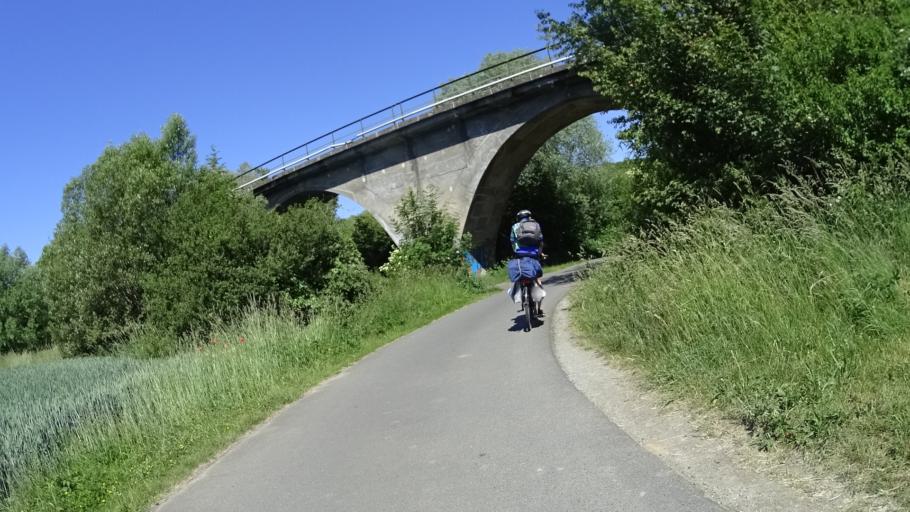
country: DE
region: Baden-Wuerttemberg
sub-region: Regierungsbezirk Stuttgart
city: Weikersheim
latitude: 49.4711
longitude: 9.8930
